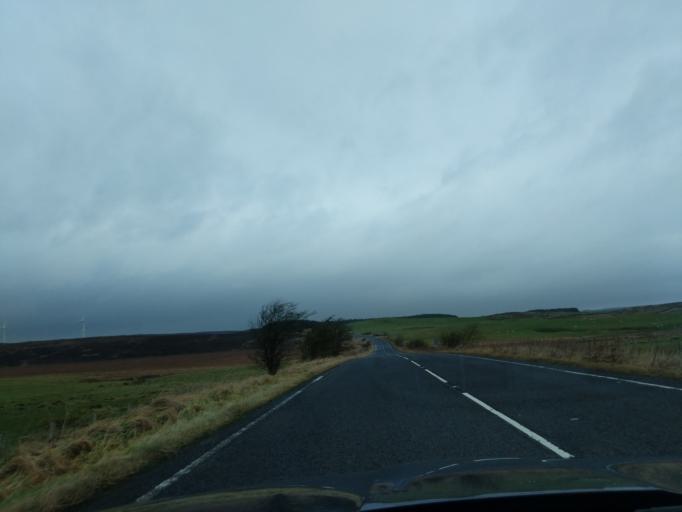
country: GB
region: England
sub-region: Northumberland
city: Rothley
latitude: 55.1707
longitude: -2.0236
